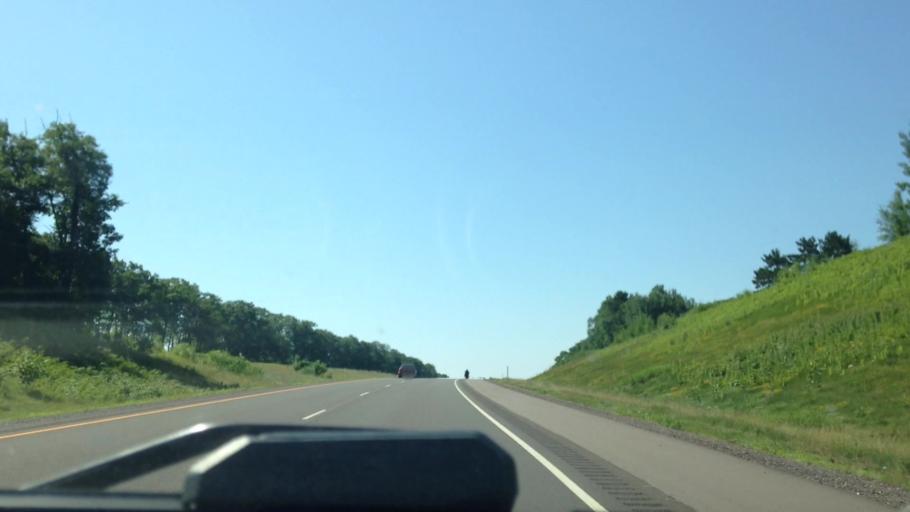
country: US
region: Wisconsin
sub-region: Washburn County
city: Spooner
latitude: 46.0060
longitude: -91.8344
